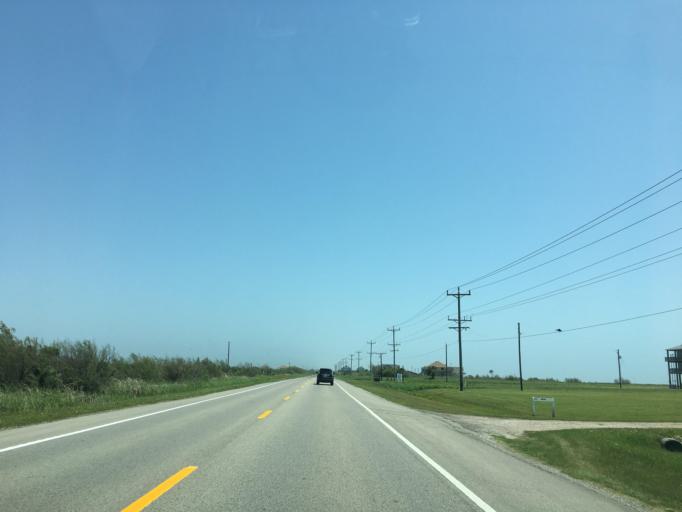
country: US
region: Texas
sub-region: Galveston County
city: Bolivar Peninsula
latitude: 29.4955
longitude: -94.5358
